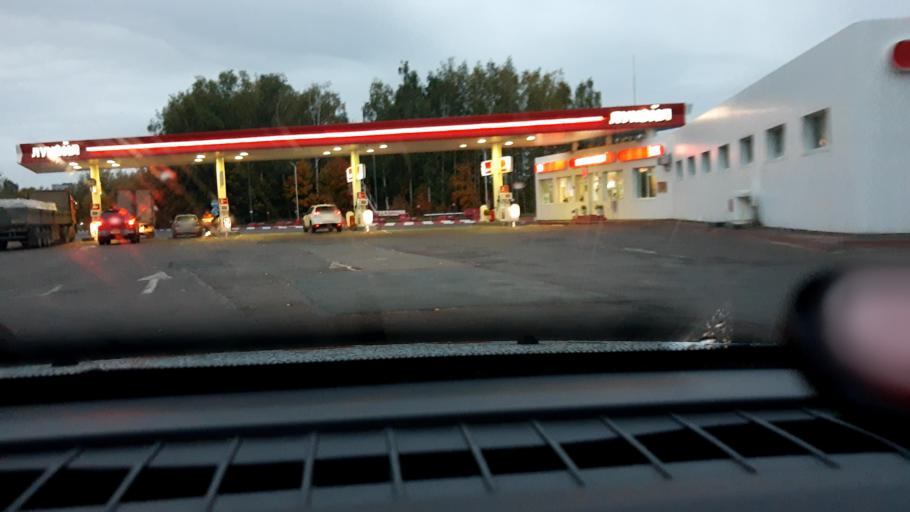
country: RU
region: Vladimir
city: Bogolyubovo
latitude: 56.1756
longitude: 40.4932
